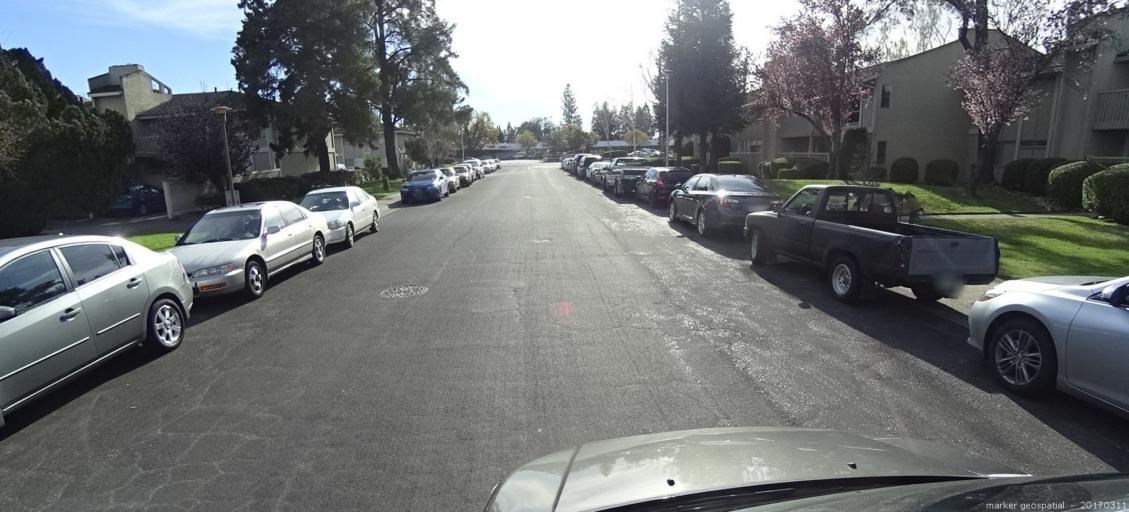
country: US
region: California
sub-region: Yolo County
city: West Sacramento
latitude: 38.5088
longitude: -121.5408
